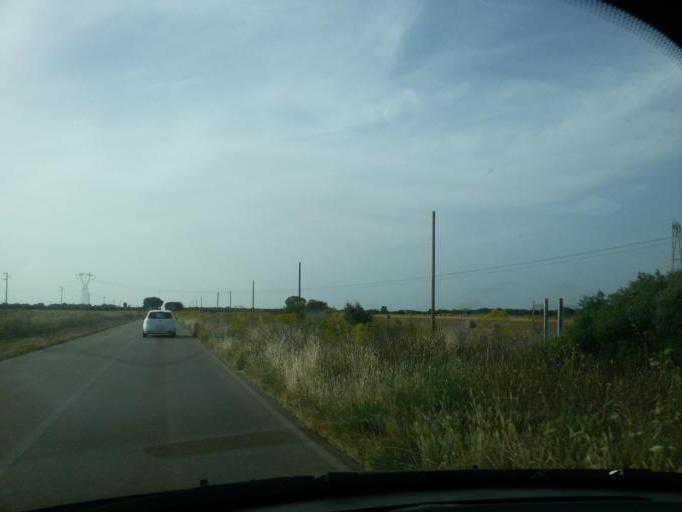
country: IT
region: Apulia
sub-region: Provincia di Brindisi
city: San Pancrazio Salentino
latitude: 40.3390
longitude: 17.8494
